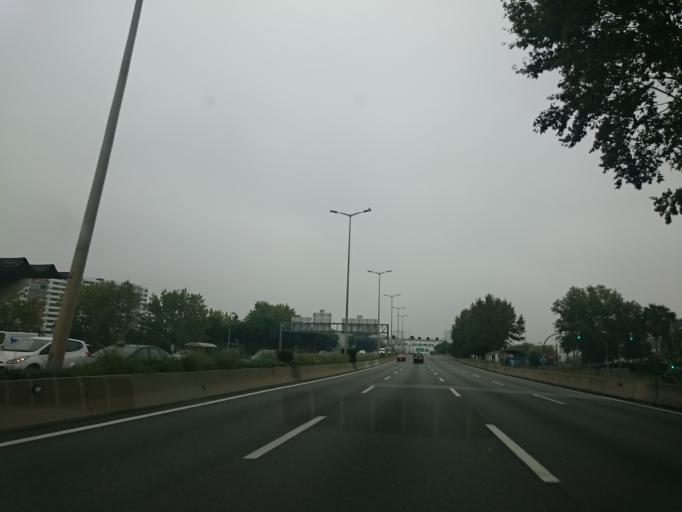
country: ES
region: Catalonia
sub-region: Provincia de Barcelona
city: L'Hospitalet de Llobregat
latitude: 41.3454
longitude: 2.1097
